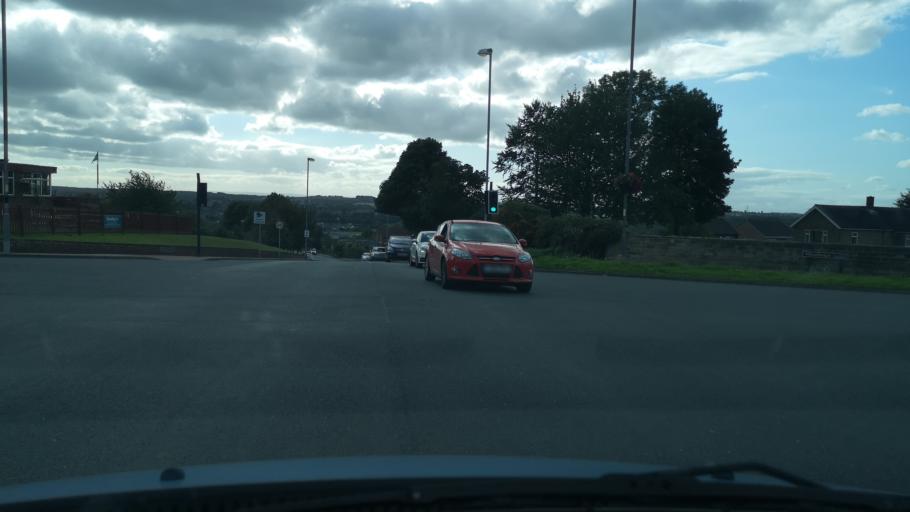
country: GB
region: England
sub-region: City and Borough of Wakefield
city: North Elmsall
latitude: 53.6040
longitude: -1.2840
